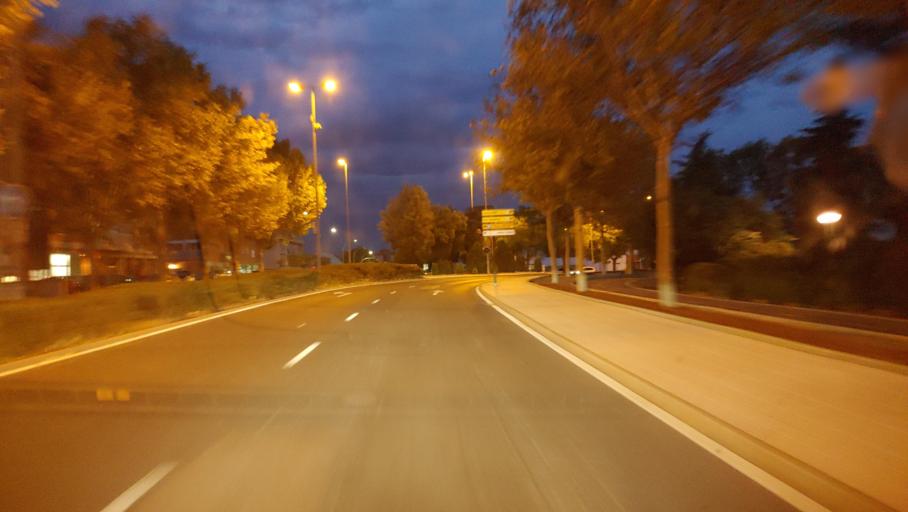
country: ES
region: Castille-La Mancha
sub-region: Provincia de Ciudad Real
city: Ciudad Real
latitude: 38.9776
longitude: -3.9177
